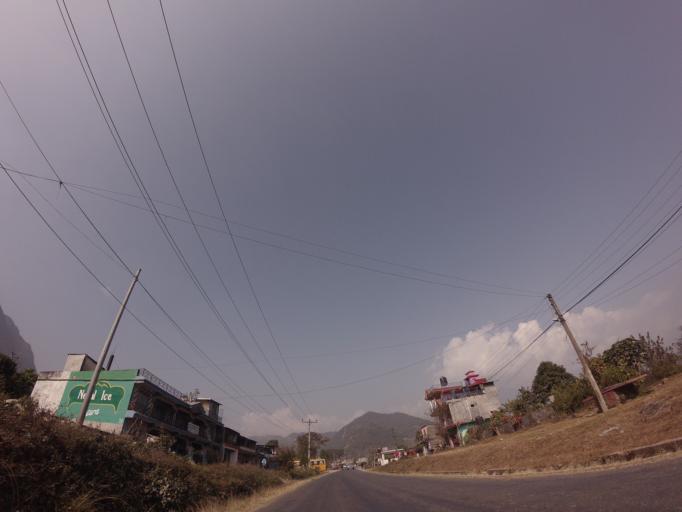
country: NP
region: Western Region
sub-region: Gandaki Zone
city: Pokhara
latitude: 28.2755
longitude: 83.9392
